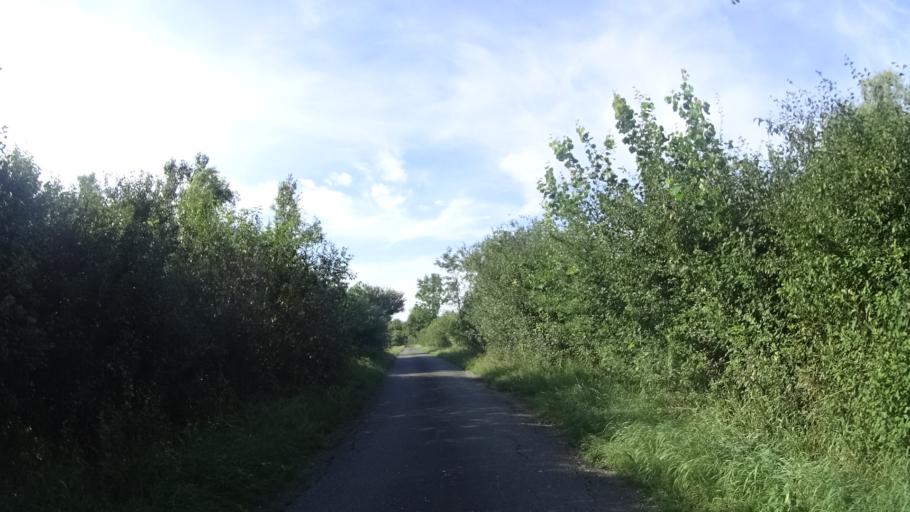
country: AT
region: Lower Austria
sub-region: Politischer Bezirk Ganserndorf
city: Drosing
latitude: 48.5626
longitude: 16.9577
